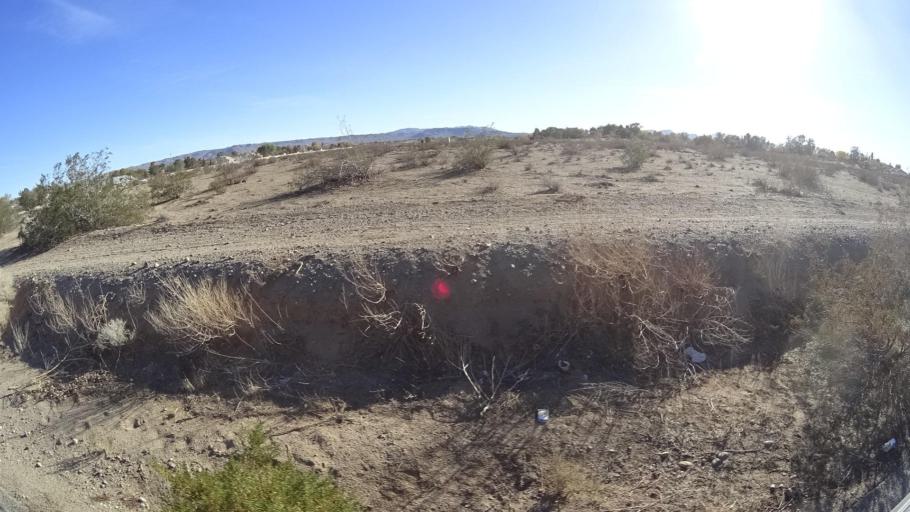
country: US
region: California
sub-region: Kern County
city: Ridgecrest
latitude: 35.6370
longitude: -117.6985
